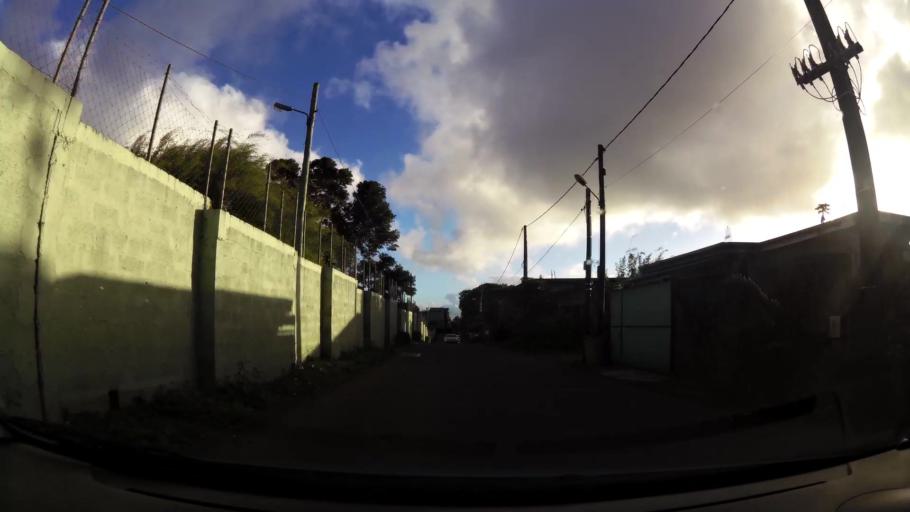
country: MU
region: Plaines Wilhems
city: Curepipe
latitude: -20.3120
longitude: 57.5332
